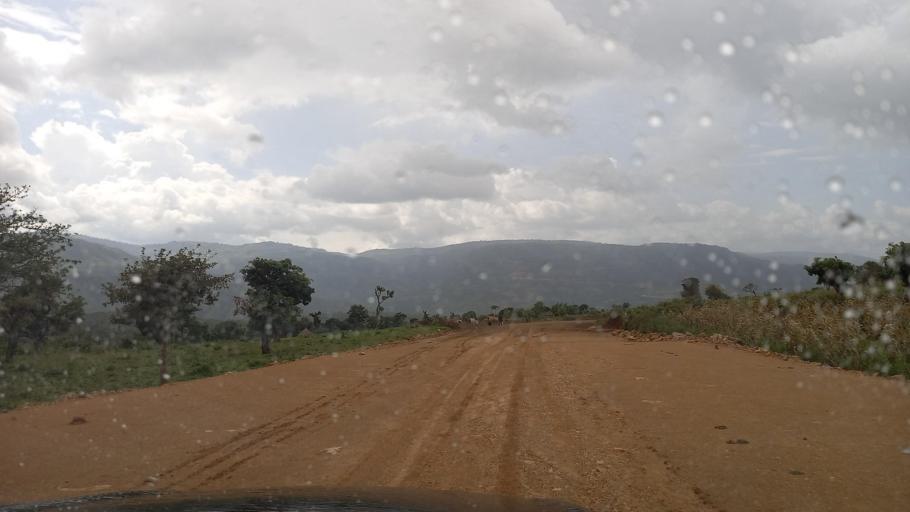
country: ET
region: Southern Nations, Nationalities, and People's Region
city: Mizan Teferi
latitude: 6.1759
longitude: 35.7053
